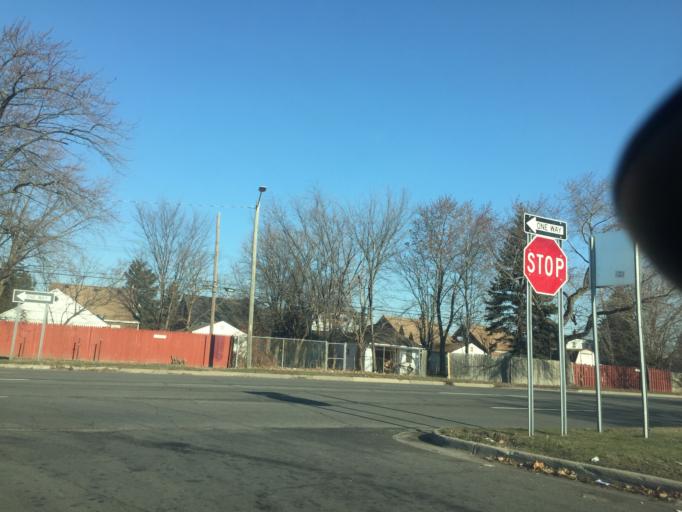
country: US
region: Michigan
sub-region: Macomb County
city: Eastpointe
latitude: 42.4502
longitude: -82.9598
